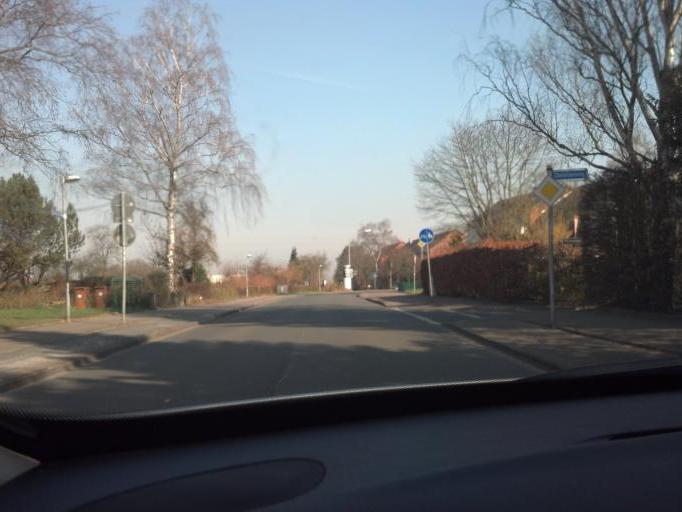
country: DE
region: Lower Saxony
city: Lueneburg
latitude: 53.2566
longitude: 10.3923
